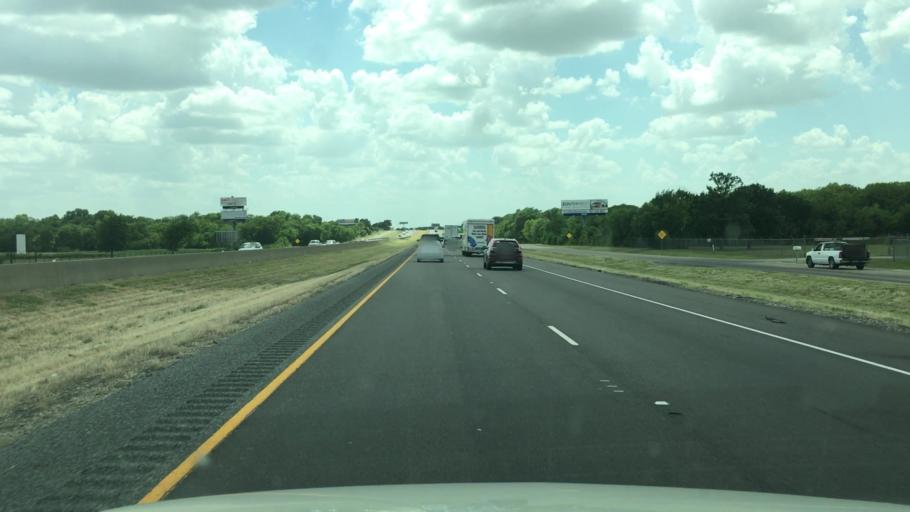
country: US
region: Texas
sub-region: Hunt County
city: Caddo Mills
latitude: 33.0590
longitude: -96.1608
